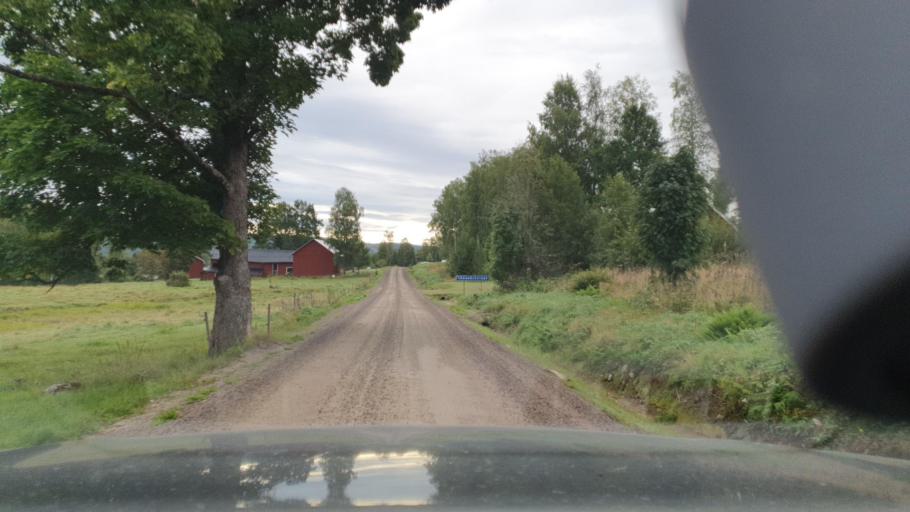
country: SE
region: Vaermland
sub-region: Torsby Kommun
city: Torsby
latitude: 59.9703
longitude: 12.8669
